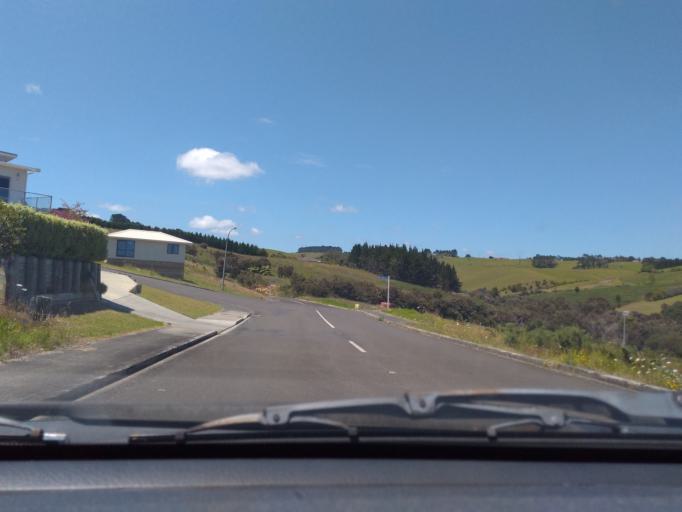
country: NZ
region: Northland
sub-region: Far North District
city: Taipa
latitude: -34.9944
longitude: 173.5056
